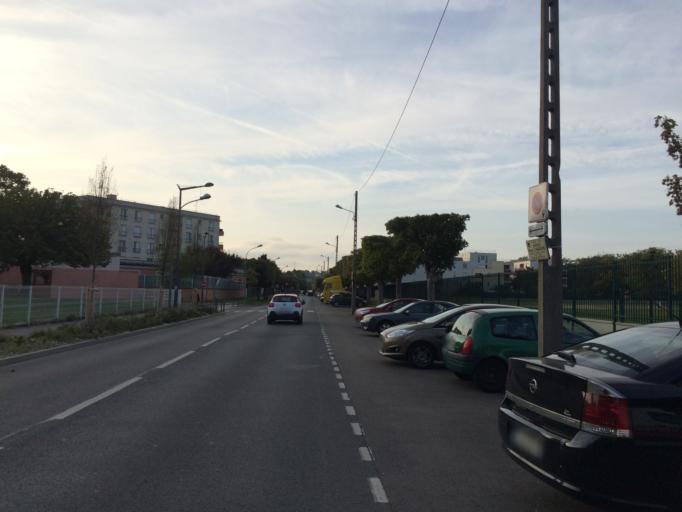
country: FR
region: Ile-de-France
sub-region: Departement de l'Essonne
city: Vigneux-sur-Seine
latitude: 48.7070
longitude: 2.4208
